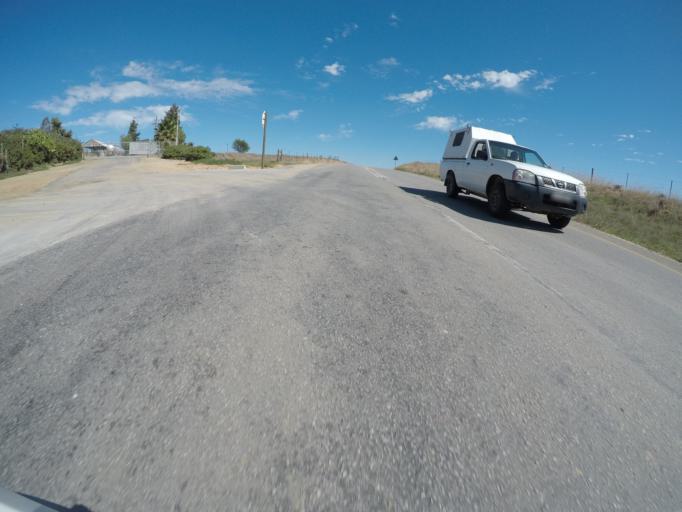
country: ZA
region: Western Cape
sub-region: West Coast District Municipality
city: Malmesbury
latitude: -33.4791
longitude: 18.7122
